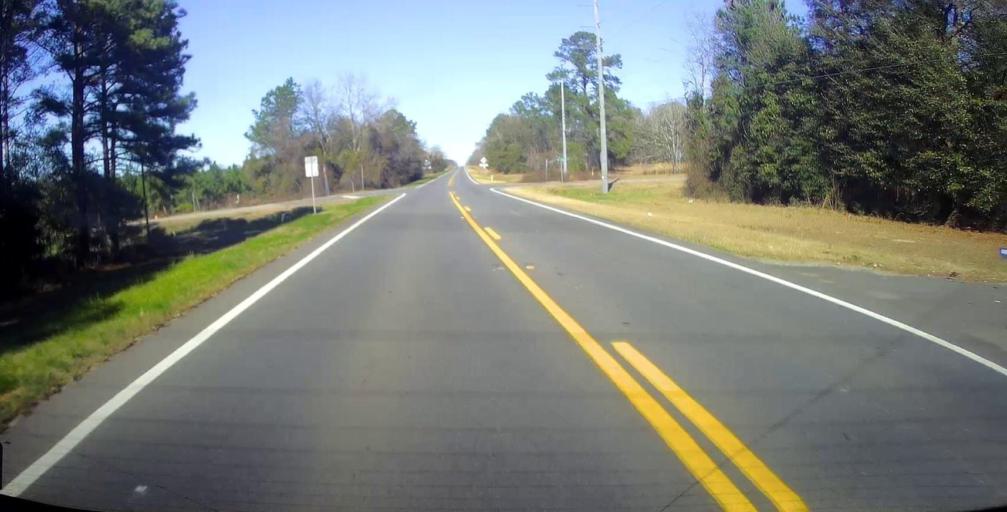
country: US
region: Georgia
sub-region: Macon County
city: Oglethorpe
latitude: 32.2373
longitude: -84.0947
